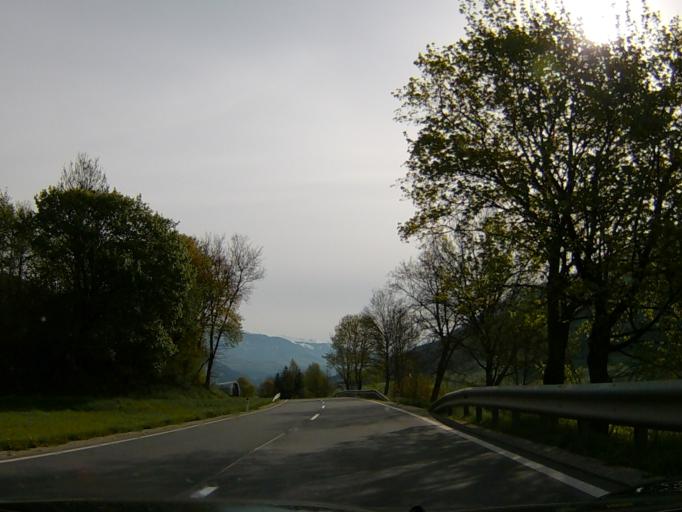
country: AT
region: Salzburg
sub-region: Politischer Bezirk Zell am See
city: Bramberg am Wildkogel
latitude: 47.2588
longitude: 12.3168
